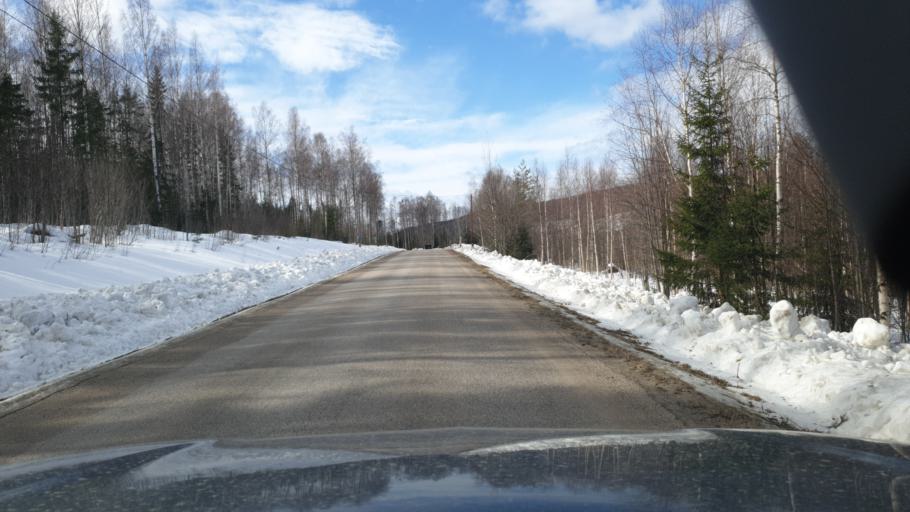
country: SE
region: Gaevleborg
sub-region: Ljusdals Kommun
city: Farila
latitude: 61.8427
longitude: 15.9071
